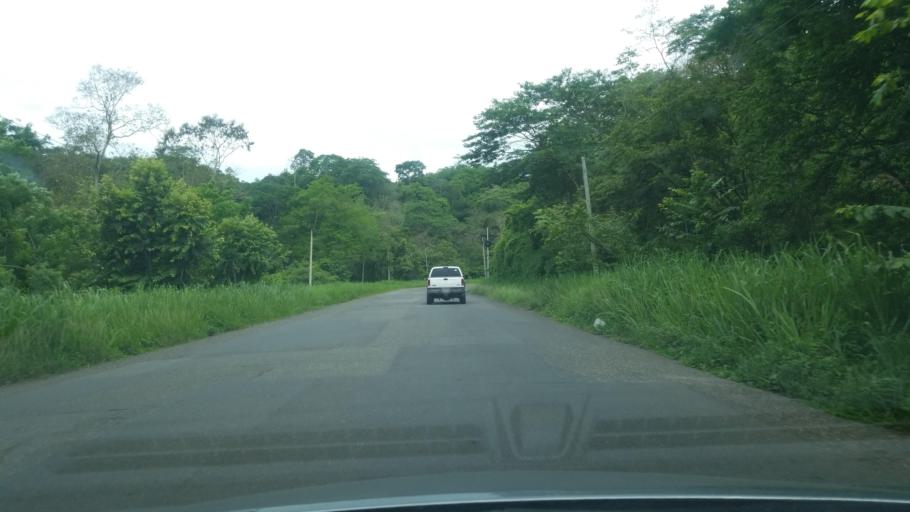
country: HN
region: Santa Barbara
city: Camalote
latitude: 15.3271
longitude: -88.2905
